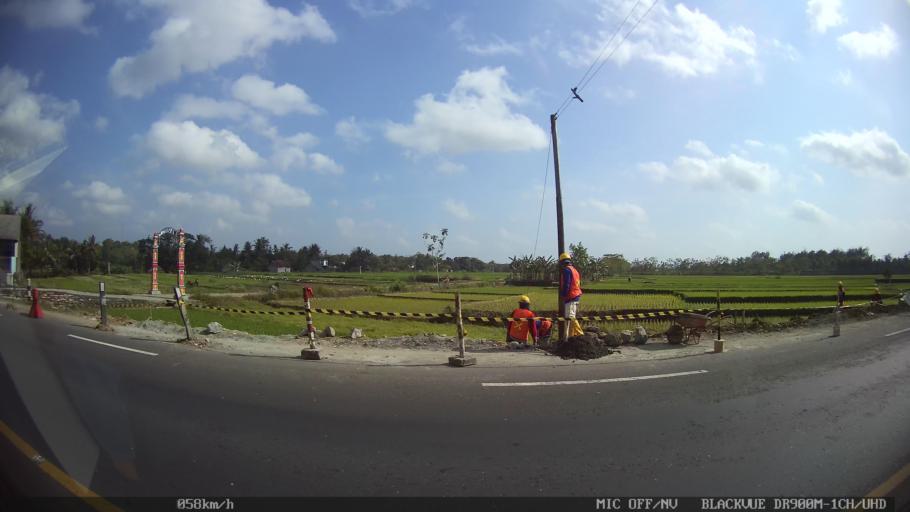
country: ID
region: Daerah Istimewa Yogyakarta
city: Godean
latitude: -7.8147
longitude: 110.2550
